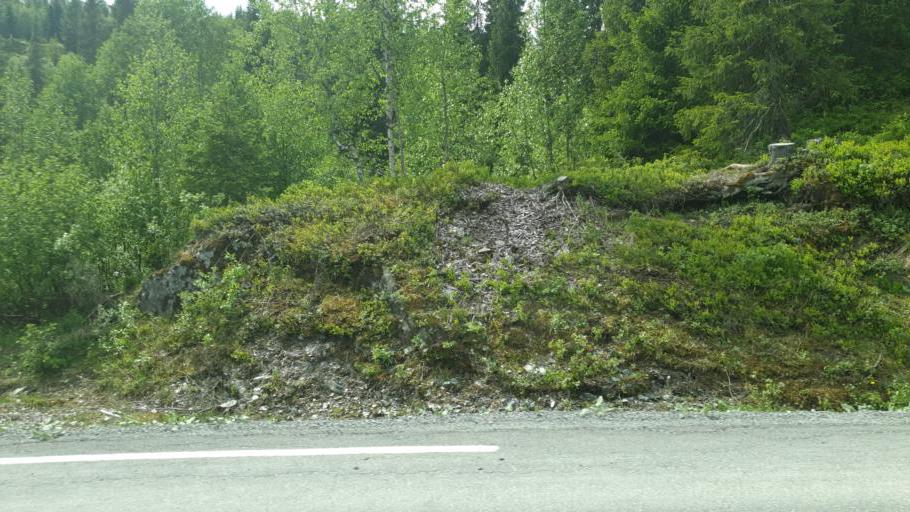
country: NO
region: Nord-Trondelag
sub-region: Leksvik
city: Leksvik
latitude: 63.6915
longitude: 10.5151
